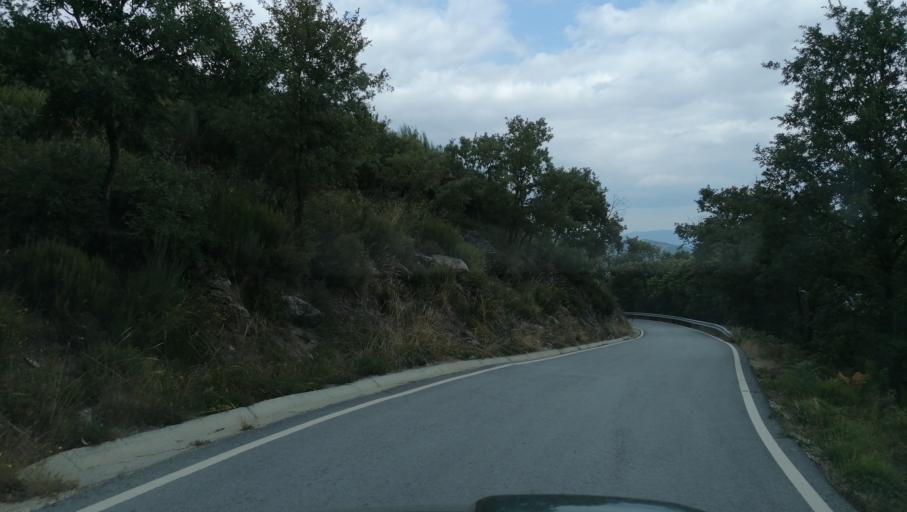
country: PT
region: Vila Real
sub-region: Vila Pouca de Aguiar
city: Vila Pouca de Aguiar
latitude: 41.5501
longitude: -7.6550
